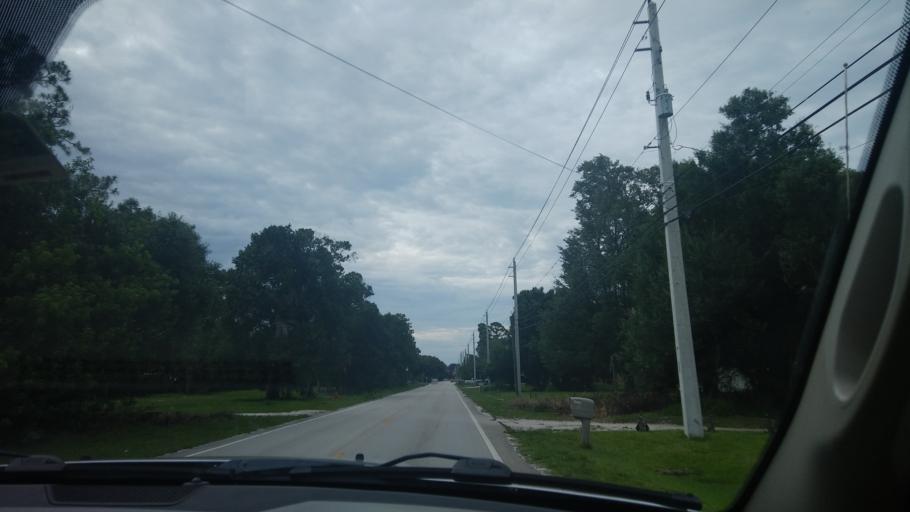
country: US
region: Florida
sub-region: Indian River County
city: Fellsmere
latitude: 27.7642
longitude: -80.5932
